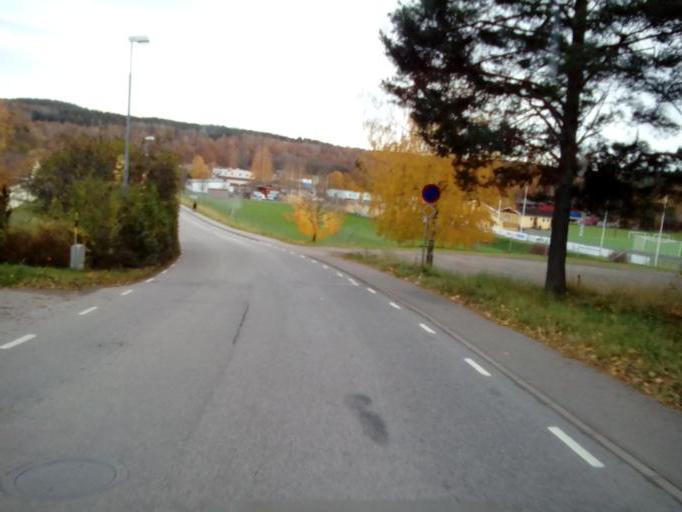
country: SE
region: OEstergoetland
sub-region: Kinda Kommun
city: Kisa
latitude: 57.9855
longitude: 15.6474
